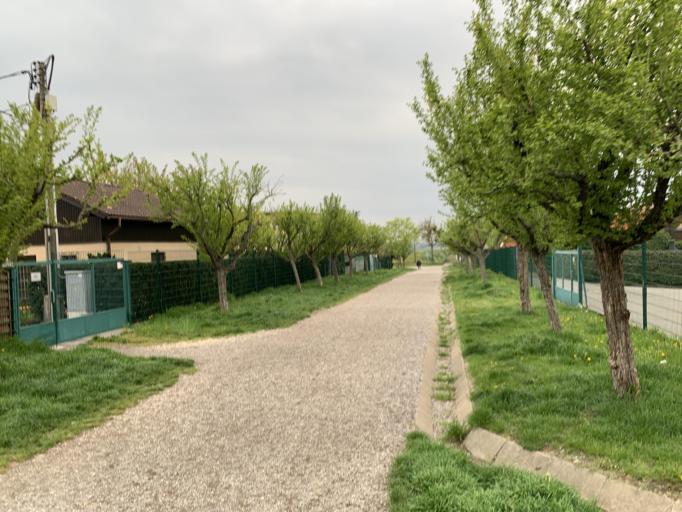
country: AT
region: Vienna
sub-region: Wien Stadt
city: Vienna
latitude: 48.1640
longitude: 16.3590
